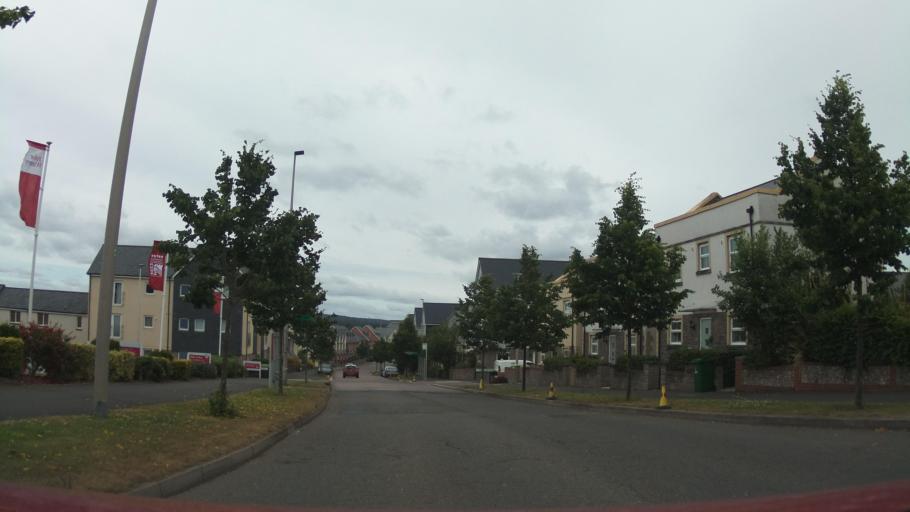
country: GB
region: England
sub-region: Devon
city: Topsham
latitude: 50.7444
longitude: -3.4166
